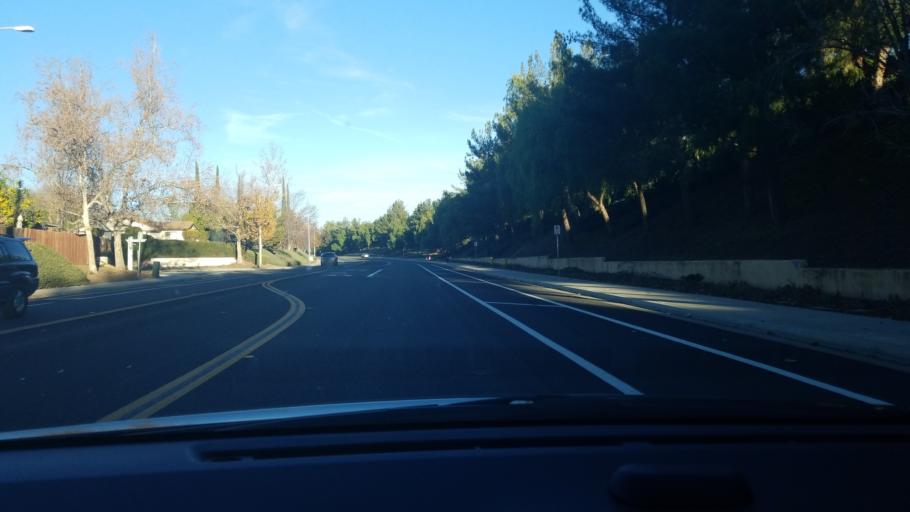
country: US
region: California
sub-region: Riverside County
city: Temecula
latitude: 33.5211
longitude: -117.1194
